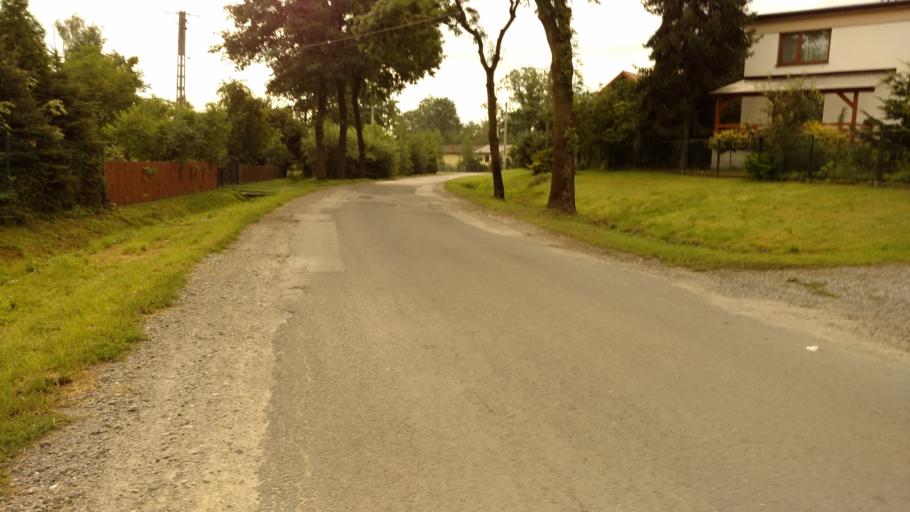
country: PL
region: Silesian Voivodeship
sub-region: Powiat pszczynski
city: Jankowice
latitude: 49.9995
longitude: 18.9993
